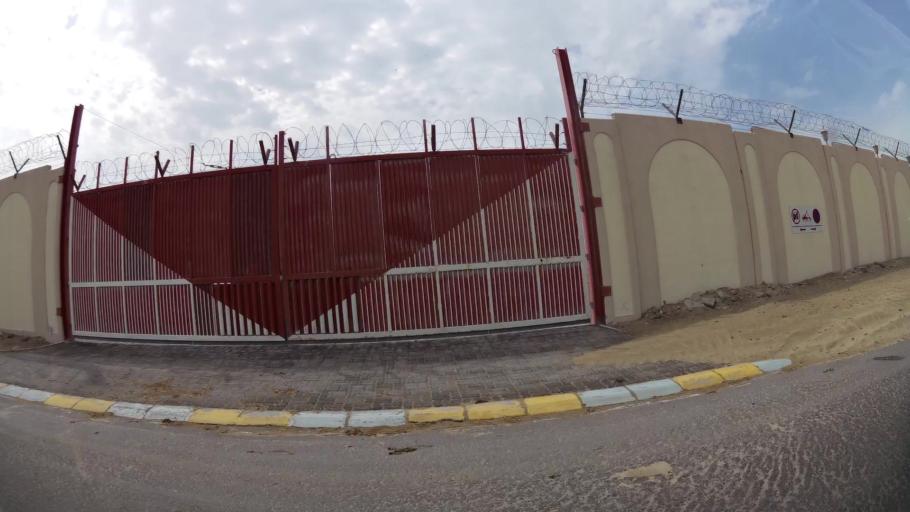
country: AE
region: Abu Dhabi
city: Abu Dhabi
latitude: 24.4273
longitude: 54.4628
